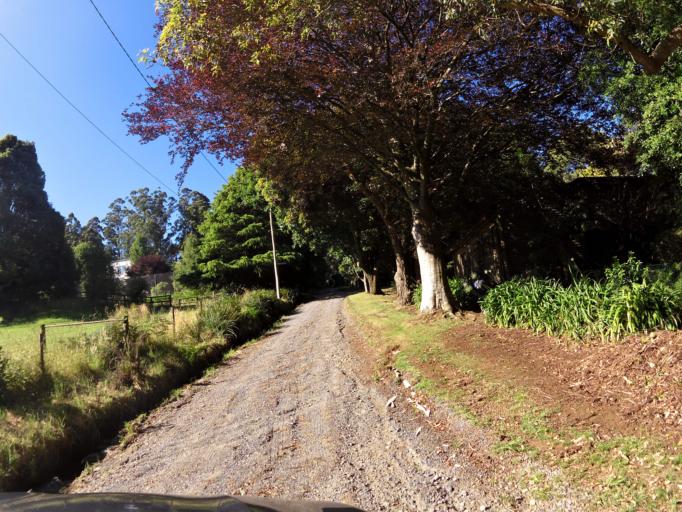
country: AU
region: Victoria
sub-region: Yarra Ranges
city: Ferny Creek
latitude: -37.8819
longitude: 145.3371
